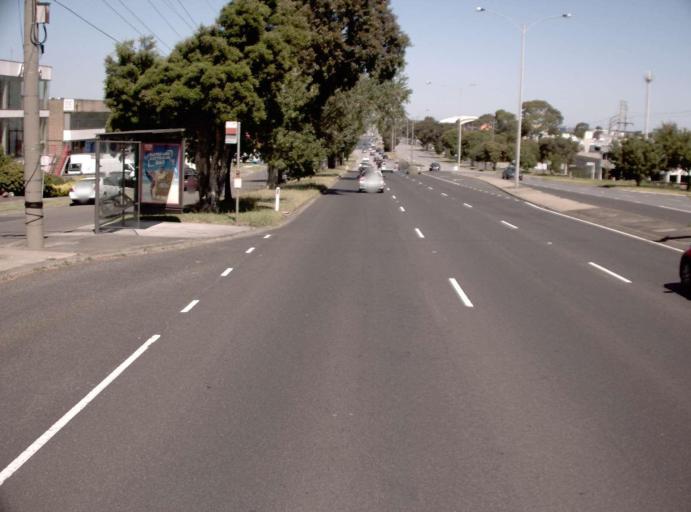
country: AU
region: Victoria
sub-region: Monash
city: Clayton
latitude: -37.9190
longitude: 145.1347
